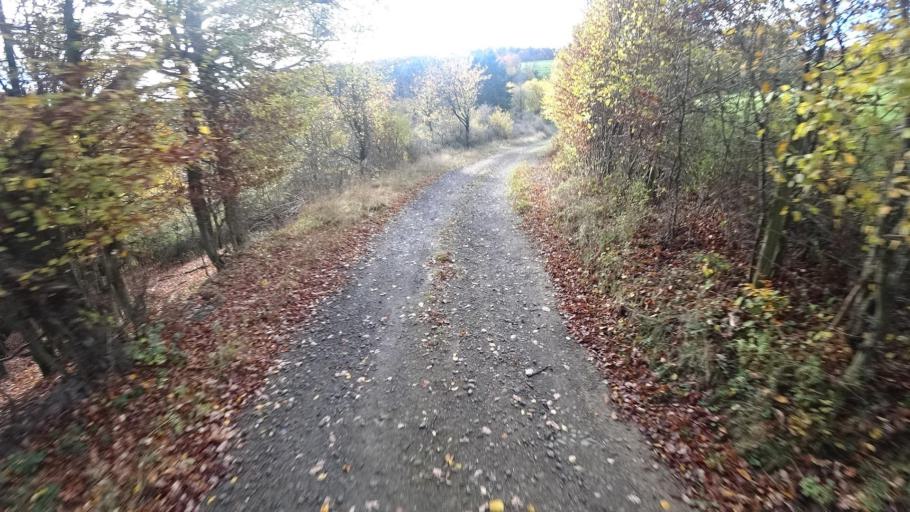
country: DE
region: Rheinland-Pfalz
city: Lind
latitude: 50.4904
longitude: 6.9416
